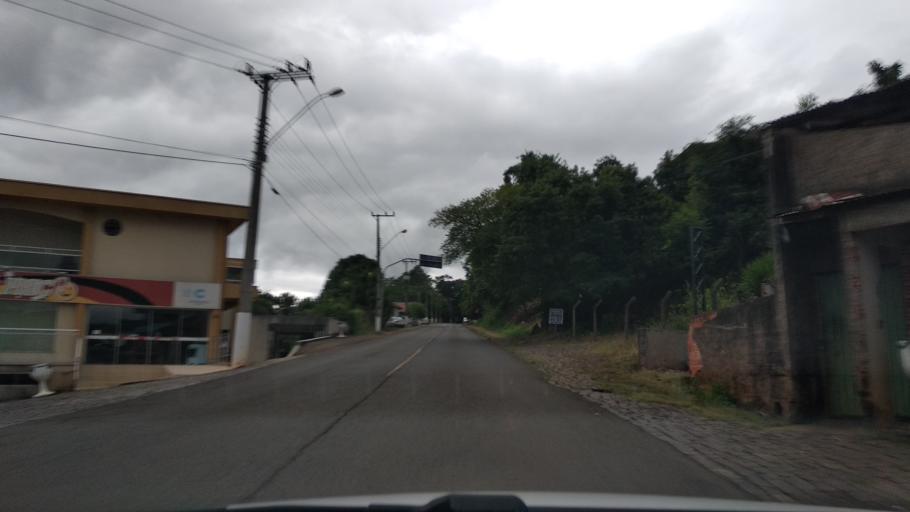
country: BR
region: Santa Catarina
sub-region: Videira
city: Videira
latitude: -27.0453
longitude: -51.2252
